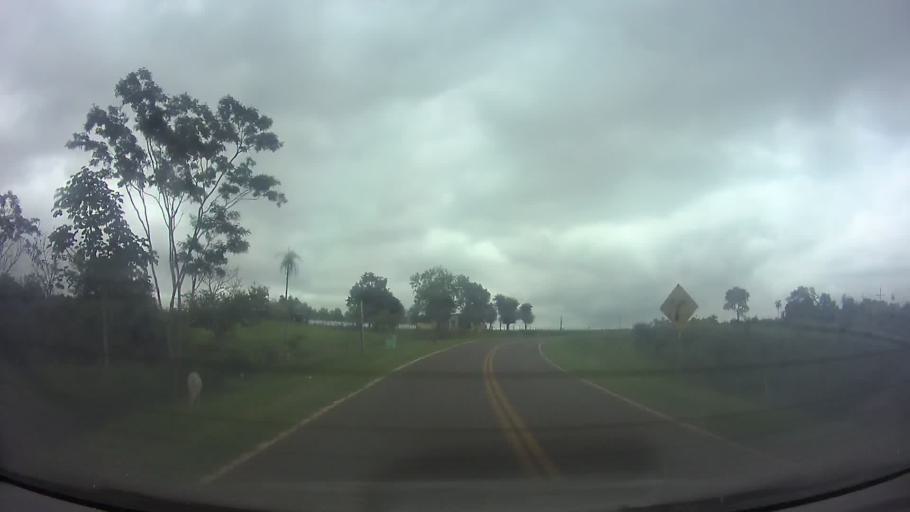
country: PY
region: Paraguari
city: Acahay
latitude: -25.9282
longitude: -57.1072
